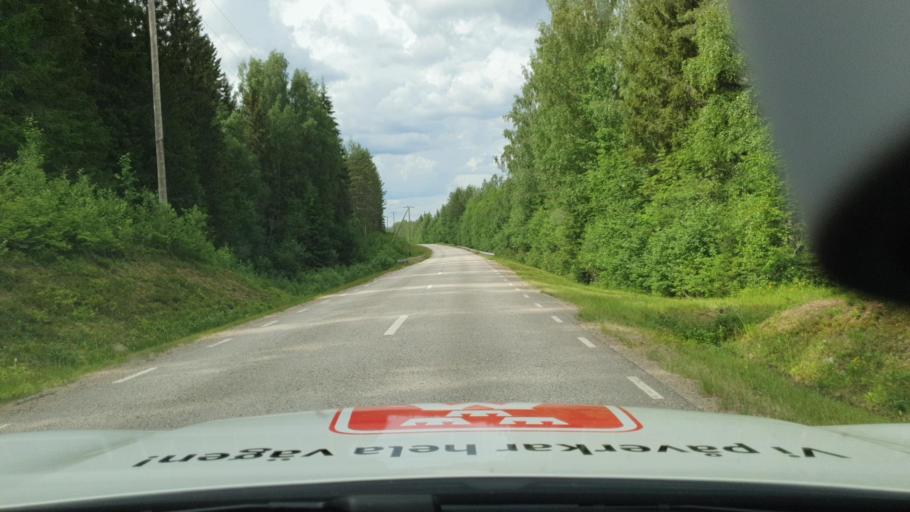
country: NO
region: Hedmark
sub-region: Trysil
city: Innbygda
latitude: 61.0065
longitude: 12.4833
